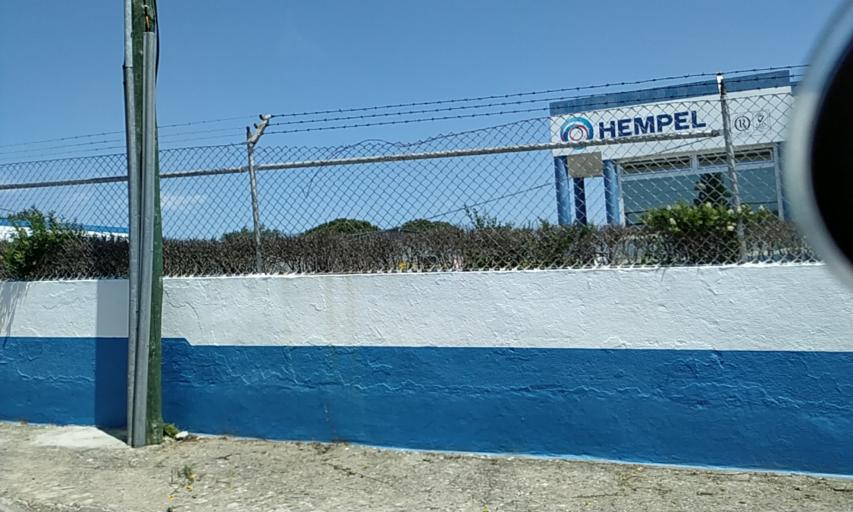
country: PT
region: Setubal
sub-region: Palmela
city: Palmela
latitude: 38.5707
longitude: -8.8724
